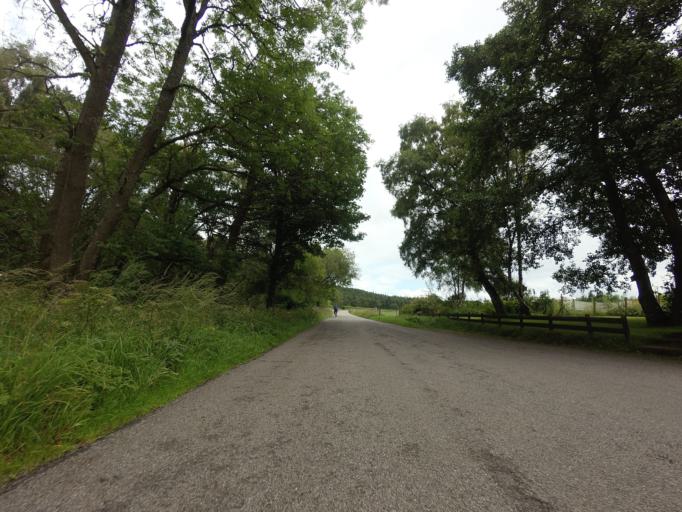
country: GB
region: Scotland
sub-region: Moray
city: Lhanbryd
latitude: 57.6659
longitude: -3.1728
